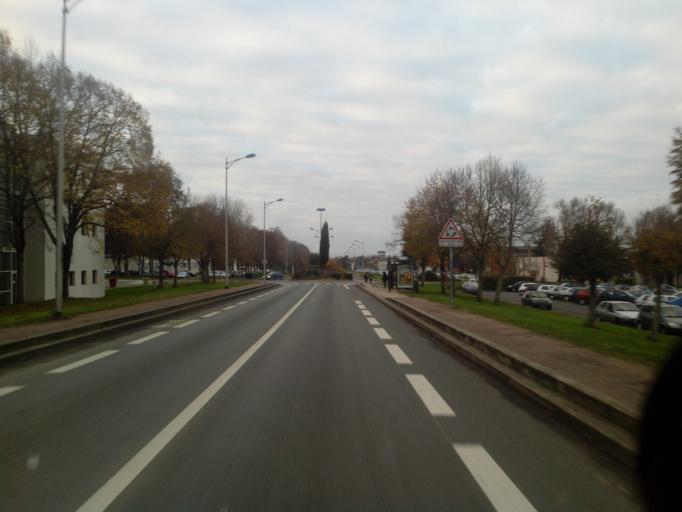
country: FR
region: Poitou-Charentes
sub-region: Departement de la Vienne
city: Mignaloux-Beauvoir
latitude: 46.5689
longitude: 0.3839
